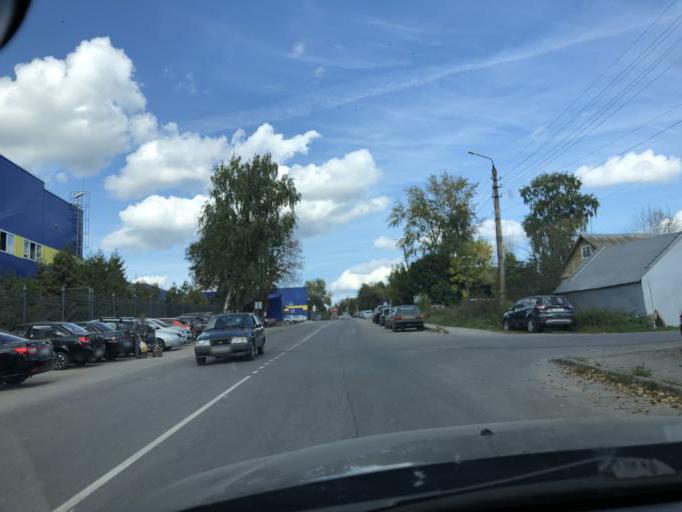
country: RU
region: Tula
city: Yasnogorsk
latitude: 54.4860
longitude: 37.6851
